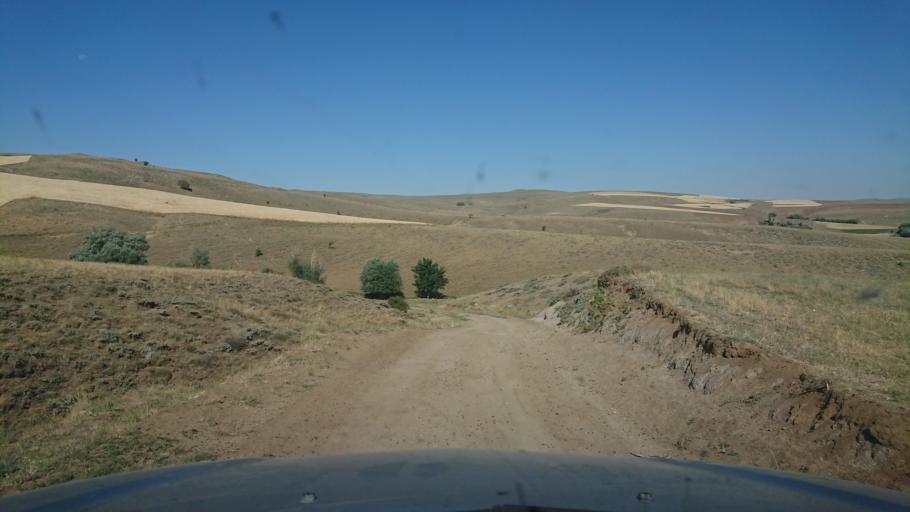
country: TR
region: Aksaray
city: Agacoren
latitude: 38.8348
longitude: 33.9287
